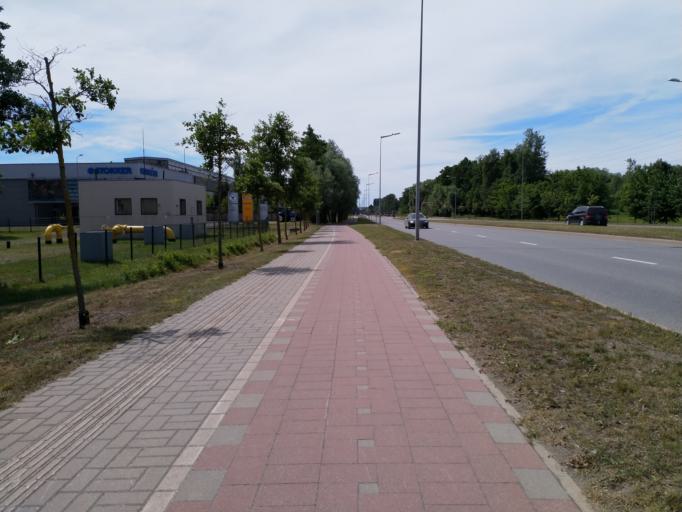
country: LV
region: Liepaja
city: Vec-Liepaja
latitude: 56.5309
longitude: 21.0432
